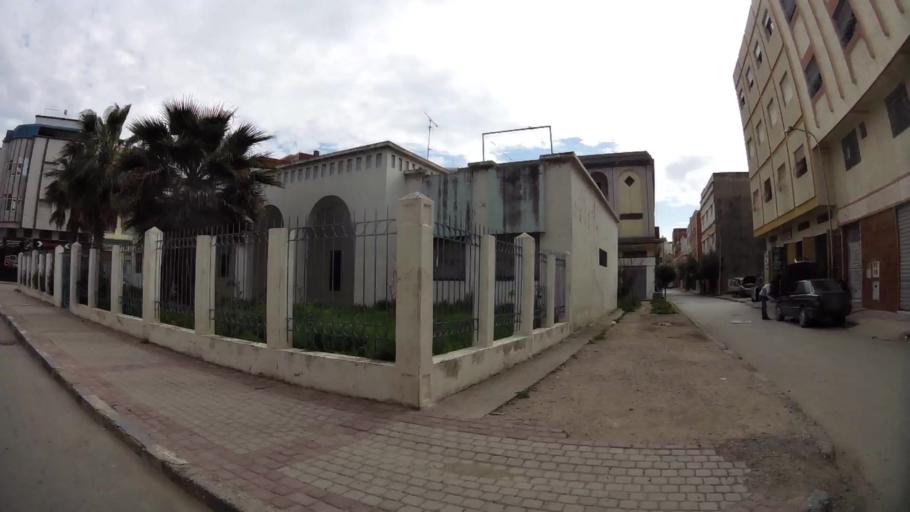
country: MA
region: Tanger-Tetouan
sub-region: Tanger-Assilah
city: Tangier
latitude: 35.7554
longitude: -5.7965
